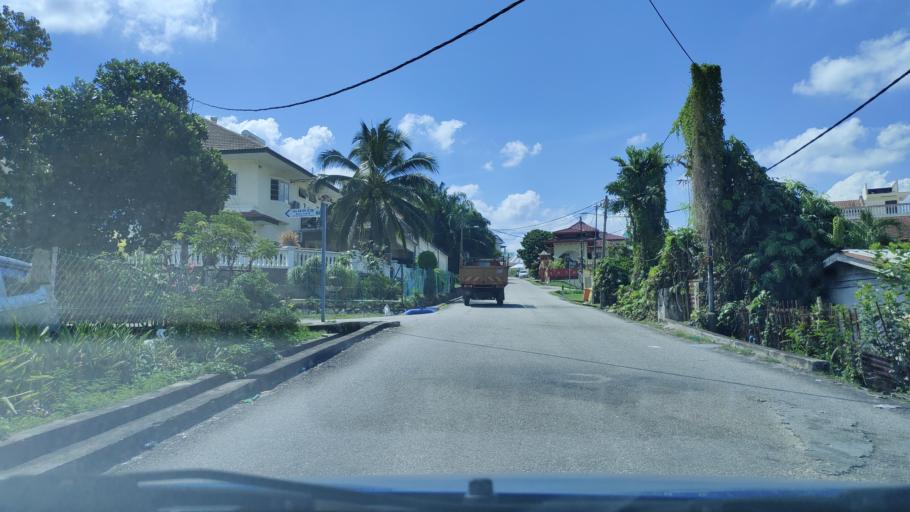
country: MY
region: Selangor
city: Kampong Baharu Balakong
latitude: 3.0281
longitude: 101.7003
